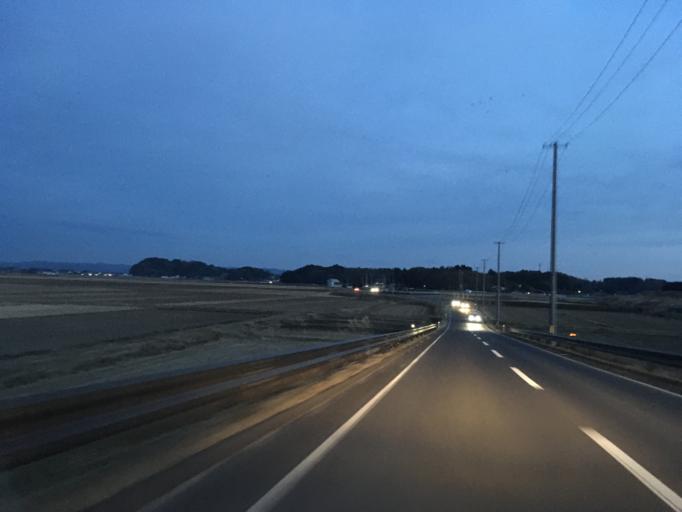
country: JP
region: Miyagi
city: Wakuya
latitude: 38.7113
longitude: 141.1488
